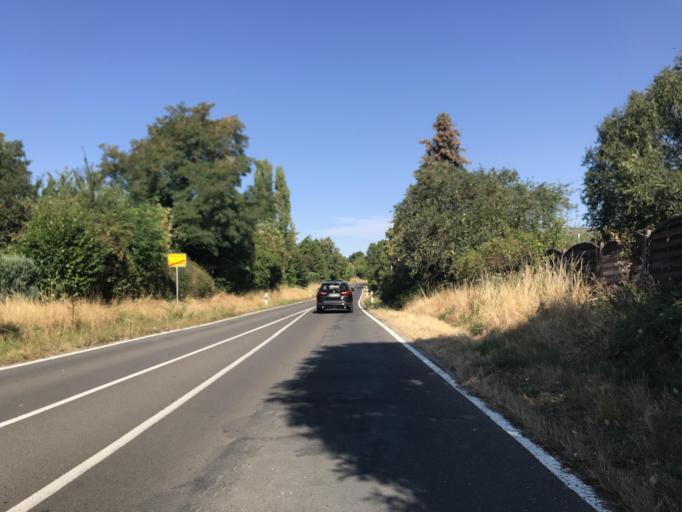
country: DE
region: Hesse
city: Geisenheim
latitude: 50.0108
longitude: 7.9736
